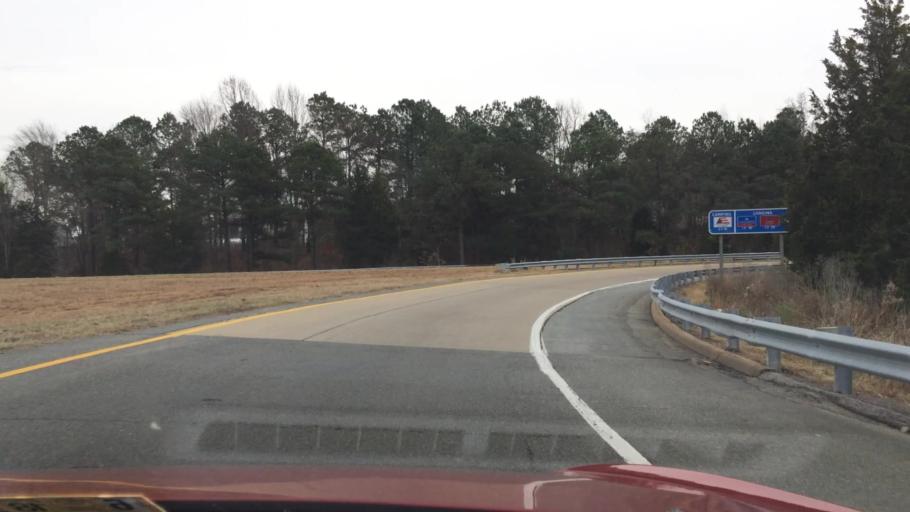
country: US
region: Virginia
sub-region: Henrico County
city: Chamberlayne
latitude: 37.6579
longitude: -77.4586
